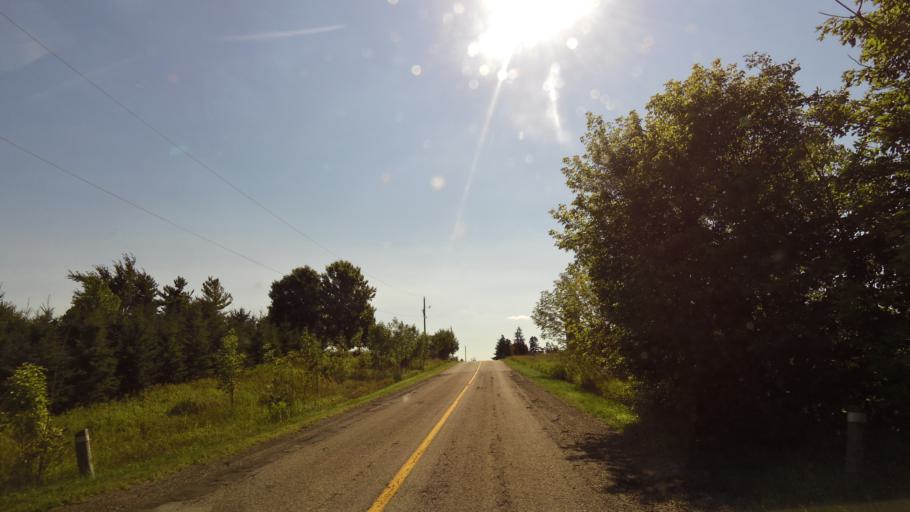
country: CA
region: Ontario
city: Brampton
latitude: 43.7627
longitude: -79.9389
